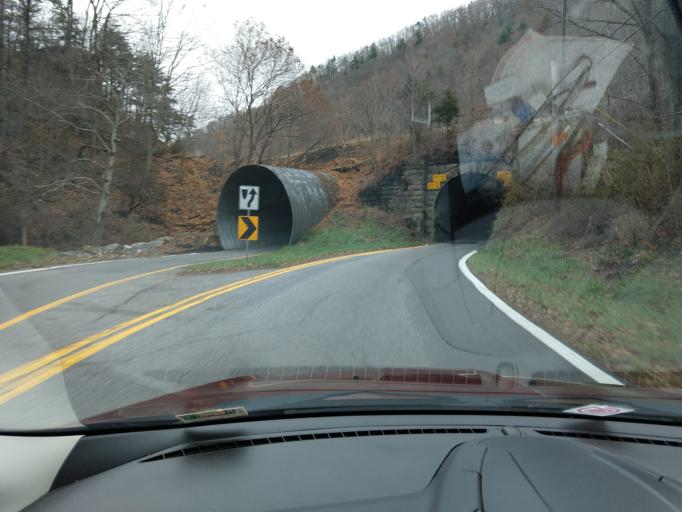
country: US
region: West Virginia
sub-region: Greenbrier County
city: White Sulphur Springs
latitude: 37.7470
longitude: -80.2401
